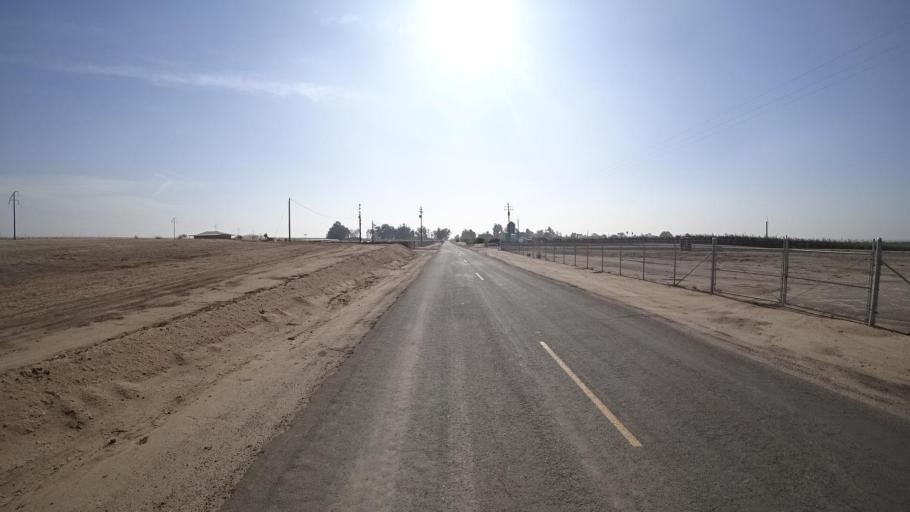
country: US
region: California
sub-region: Kern County
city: Oildale
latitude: 35.5276
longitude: -119.1083
